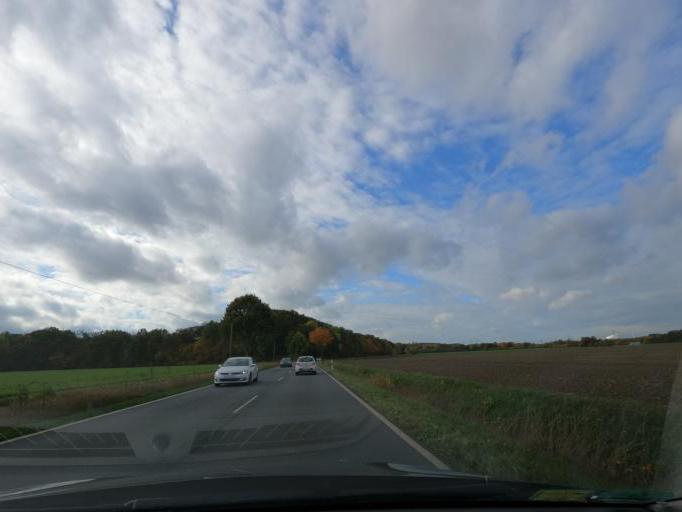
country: DE
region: Lower Saxony
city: Wolfenbuettel
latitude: 52.1376
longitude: 10.5093
